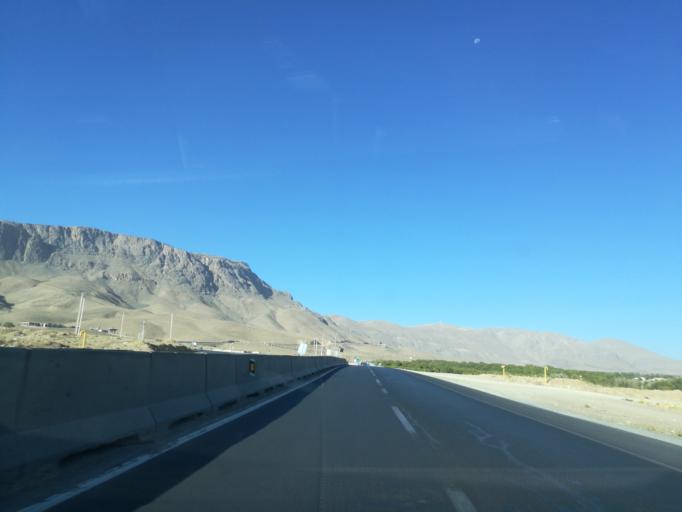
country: IR
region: Chahar Mahall va Bakhtiari
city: Farrokh Shahr
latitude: 32.3493
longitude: 51.1170
